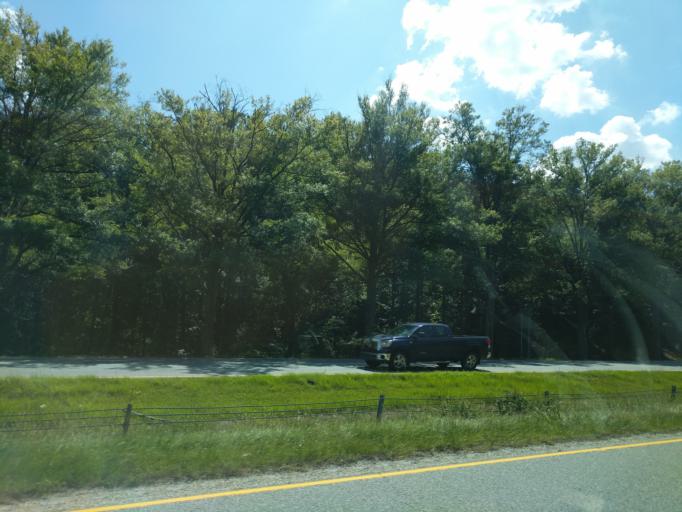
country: US
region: South Carolina
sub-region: Spartanburg County
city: Valley Falls
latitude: 34.9946
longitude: -81.9501
